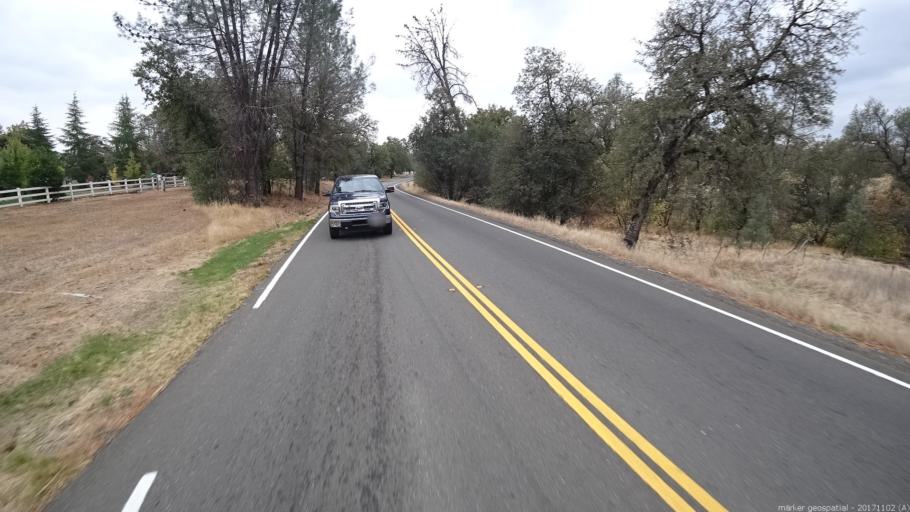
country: US
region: California
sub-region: Shasta County
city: Shasta Lake
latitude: 40.6578
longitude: -122.3298
